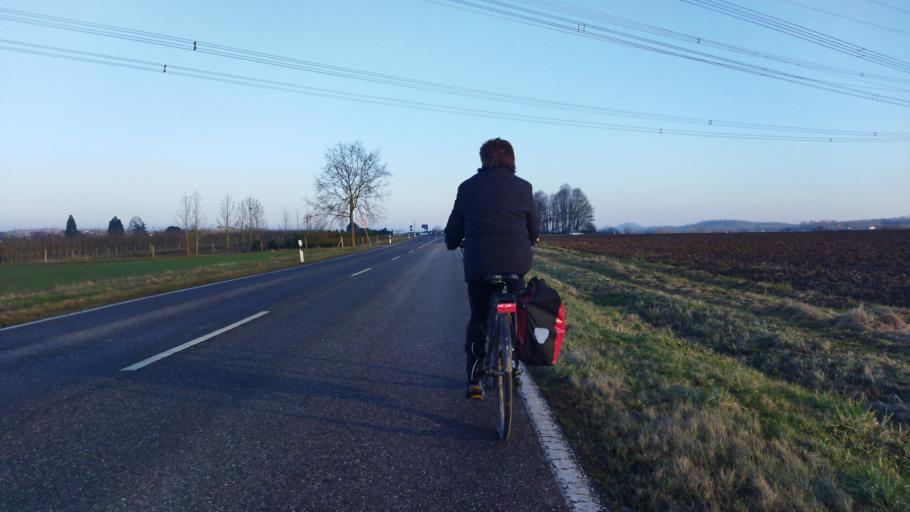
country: DE
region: Baden-Wuerttemberg
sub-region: Regierungsbezirk Stuttgart
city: Neckarwestheim
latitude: 49.0635
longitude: 9.1933
